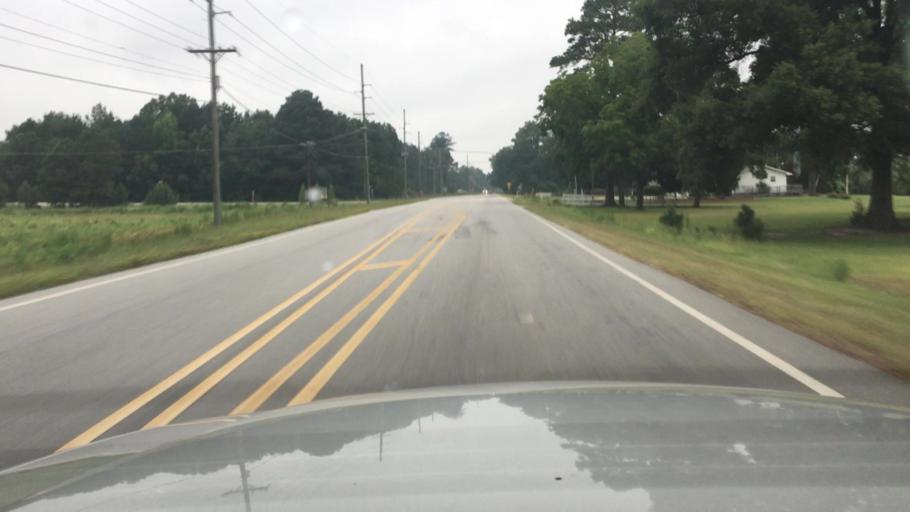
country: US
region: North Carolina
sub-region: Cumberland County
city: Fayetteville
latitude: 35.0091
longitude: -78.8634
